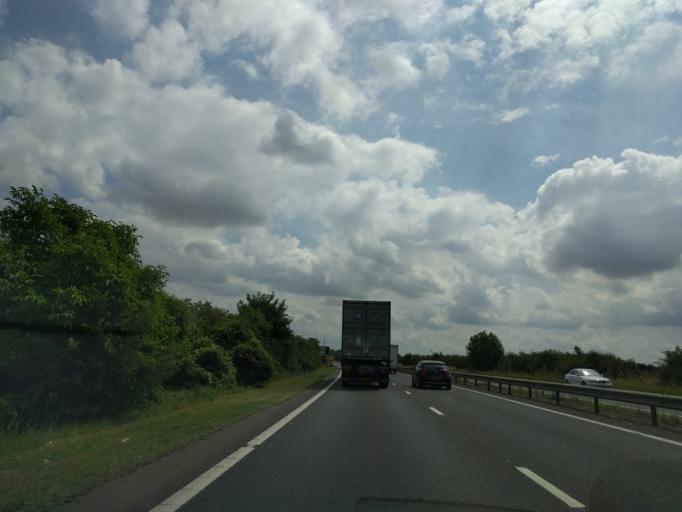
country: GB
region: England
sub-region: Cambridgeshire
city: Fulbourn
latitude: 52.2167
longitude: 0.1955
